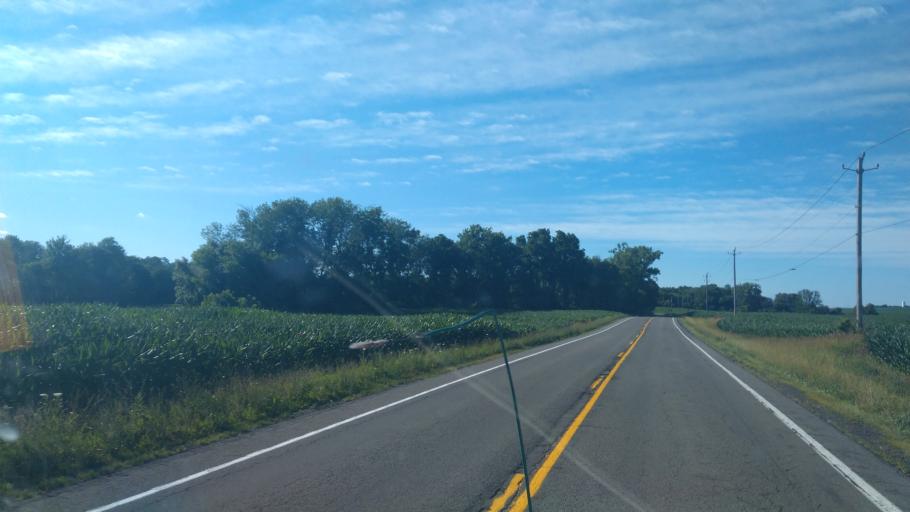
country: US
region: New York
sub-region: Wayne County
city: Lyons
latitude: 43.0161
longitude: -76.9853
